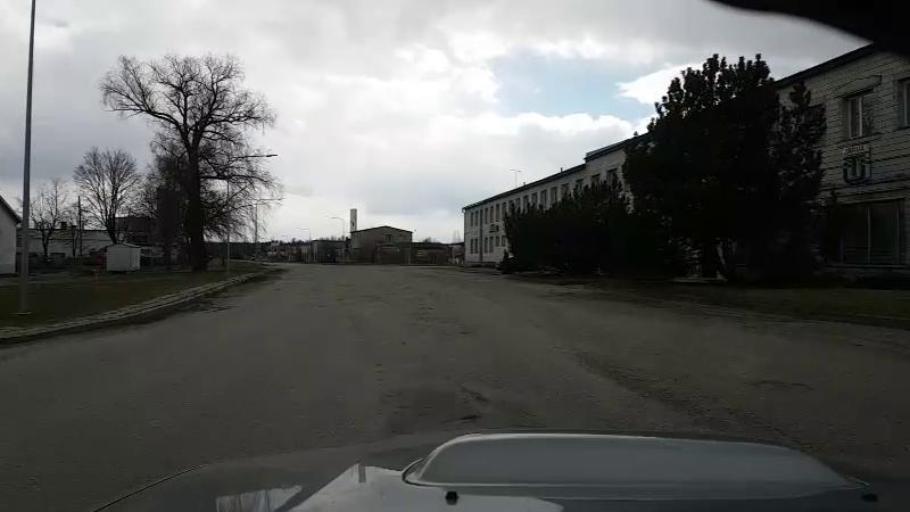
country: EE
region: Jaervamaa
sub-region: Paide linn
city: Paide
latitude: 58.8825
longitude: 25.5600
